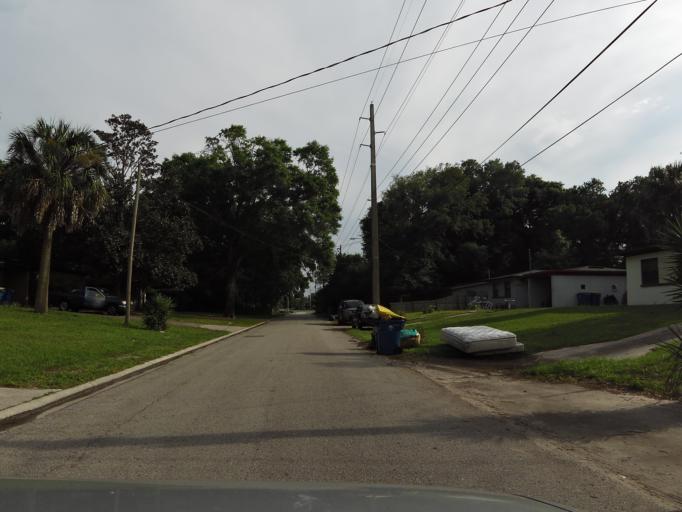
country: US
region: Florida
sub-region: Duval County
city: Jacksonville
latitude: 30.3305
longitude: -81.5915
